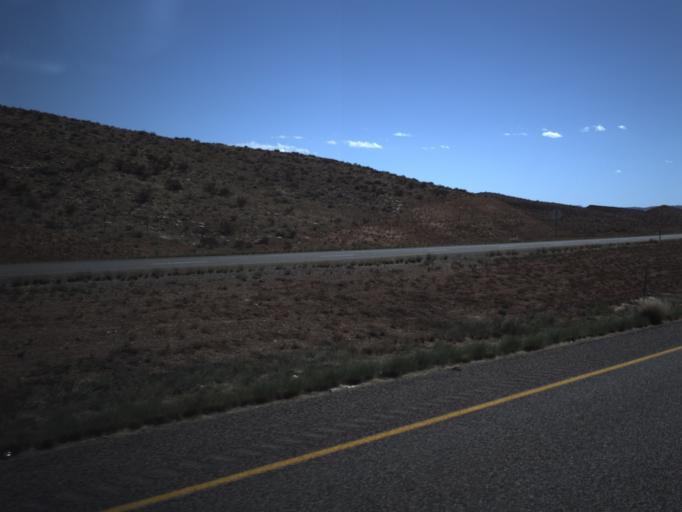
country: US
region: Utah
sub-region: Washington County
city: Saint George
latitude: 37.0206
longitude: -113.5992
